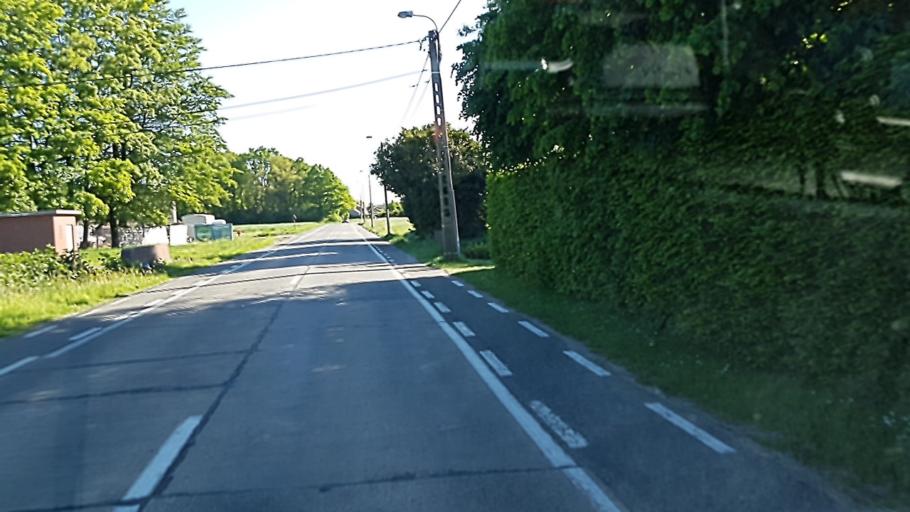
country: BE
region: Flanders
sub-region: Provincie Antwerpen
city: Herenthout
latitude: 51.1095
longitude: 4.7447
